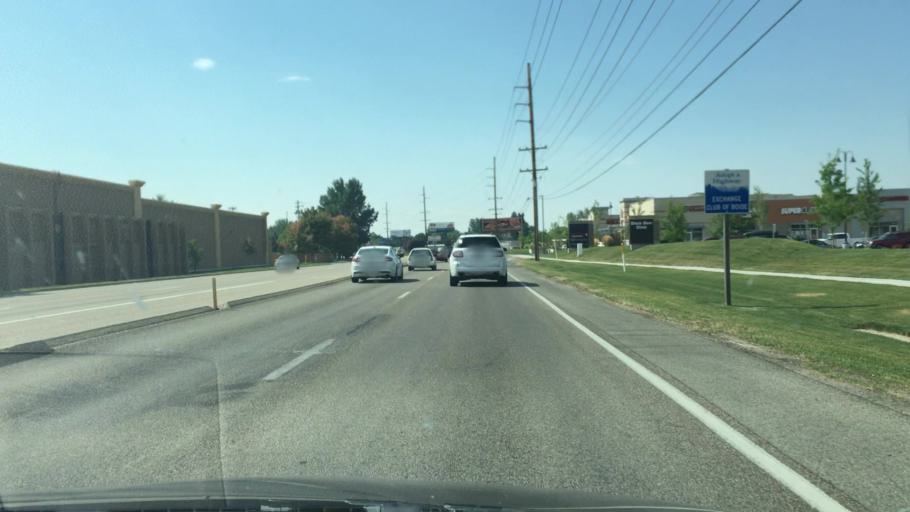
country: US
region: Idaho
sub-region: Ada County
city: Garden City
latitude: 43.6703
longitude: -116.2821
